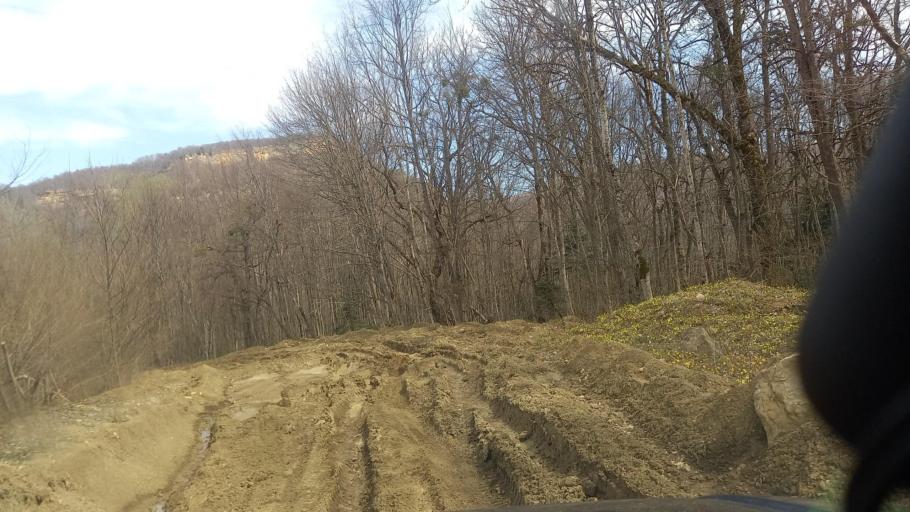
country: RU
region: Adygeya
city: Kamennomostskiy
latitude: 44.1087
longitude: 40.0920
